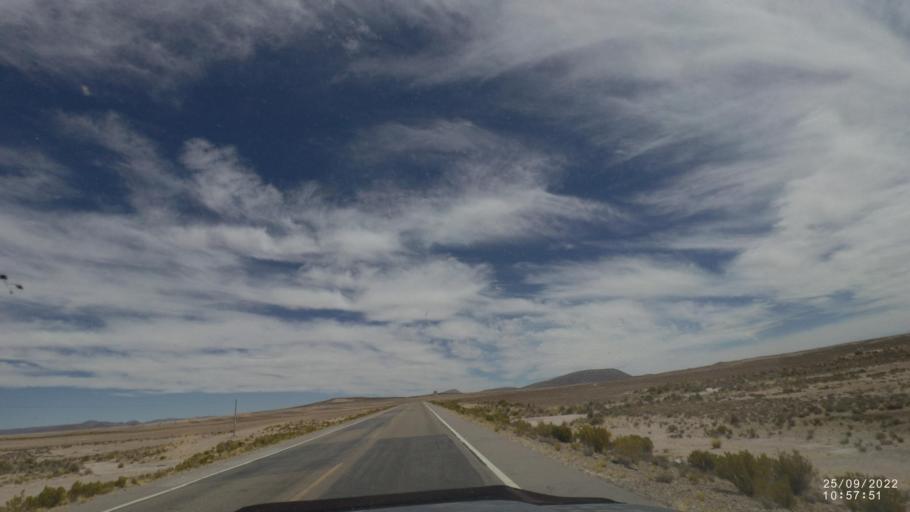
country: BO
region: Oruro
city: Challapata
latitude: -19.4706
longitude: -66.8976
